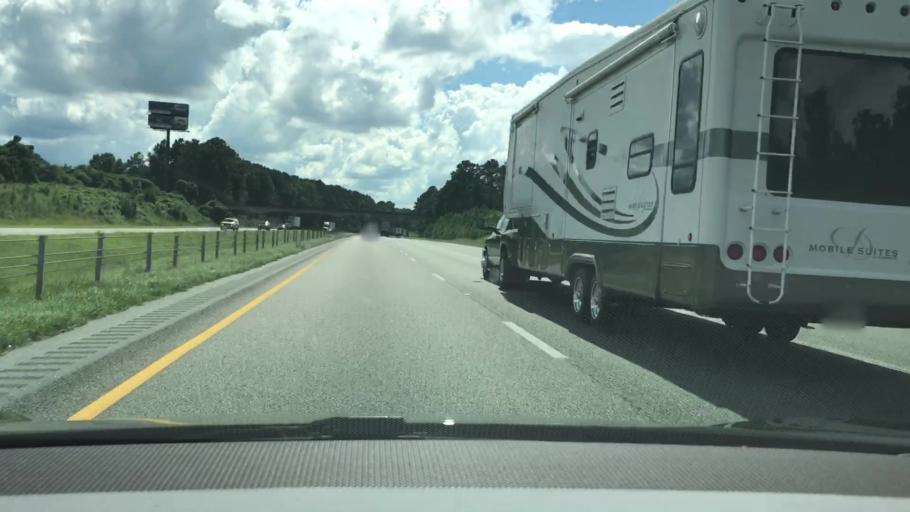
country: US
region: Alabama
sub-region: Lee County
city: Auburn
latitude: 32.5445
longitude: -85.5322
